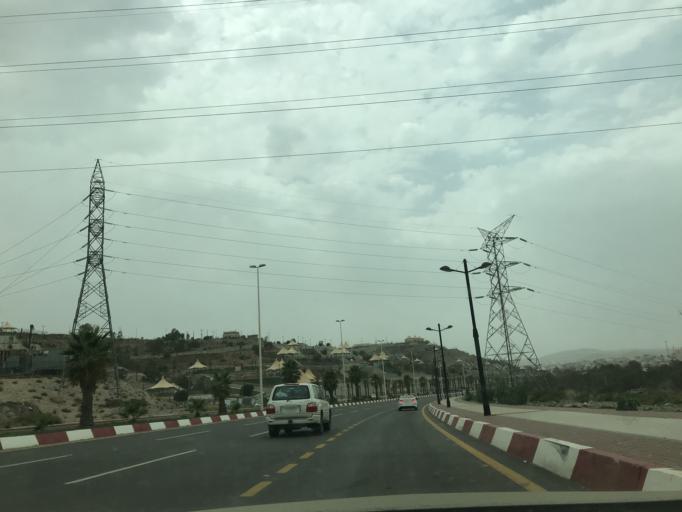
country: SA
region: Mintaqat al Bahah
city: Al Bahah
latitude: 19.8428
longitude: 41.5891
